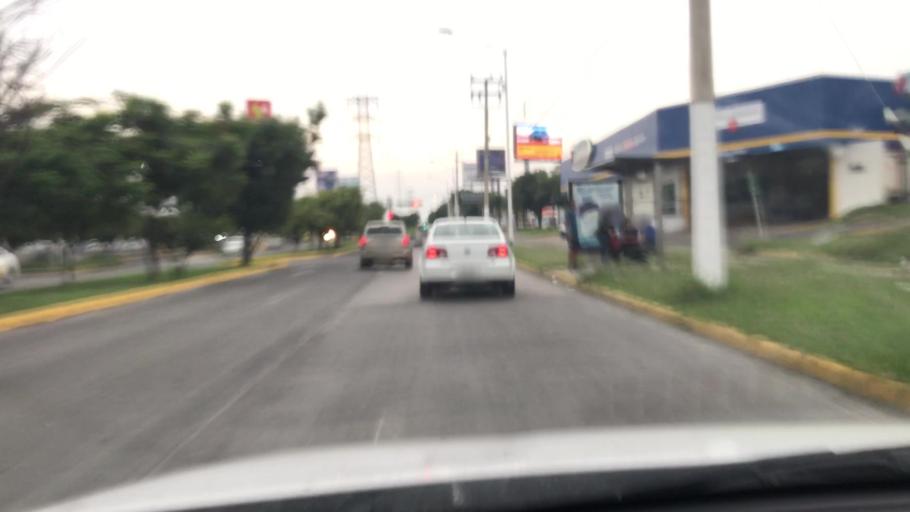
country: MX
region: Jalisco
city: Guadalajara
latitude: 20.6596
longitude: -103.4226
